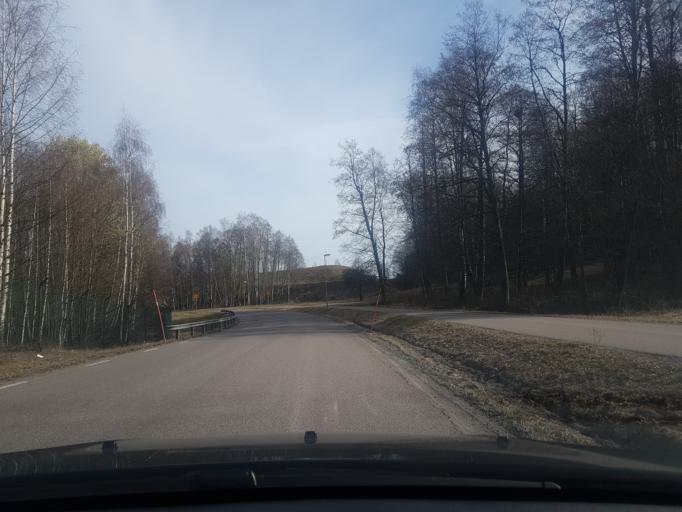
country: SE
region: Dalarna
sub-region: Borlange Kommun
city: Borlaenge
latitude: 60.4908
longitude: 15.4618
